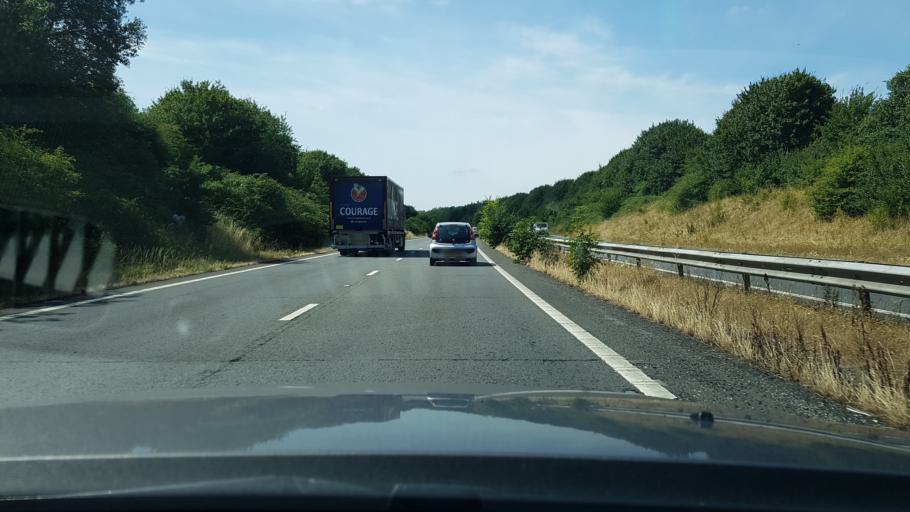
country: GB
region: England
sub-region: Hampshire
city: Emsworth
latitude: 50.8562
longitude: -0.9201
